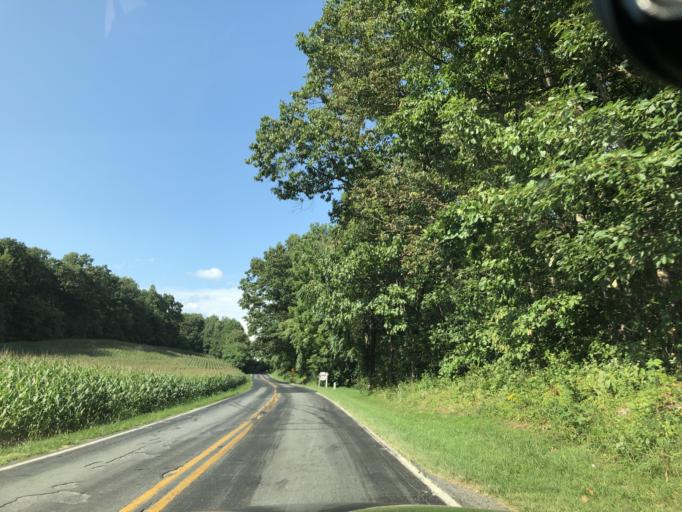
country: US
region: Maryland
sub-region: Frederick County
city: Linganore
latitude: 39.4432
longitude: -77.1766
